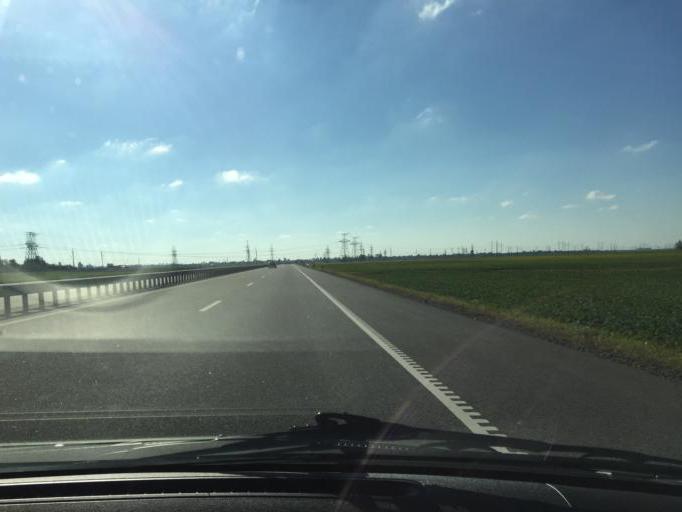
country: BY
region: Minsk
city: Slutsk
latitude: 53.0622
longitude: 27.5471
